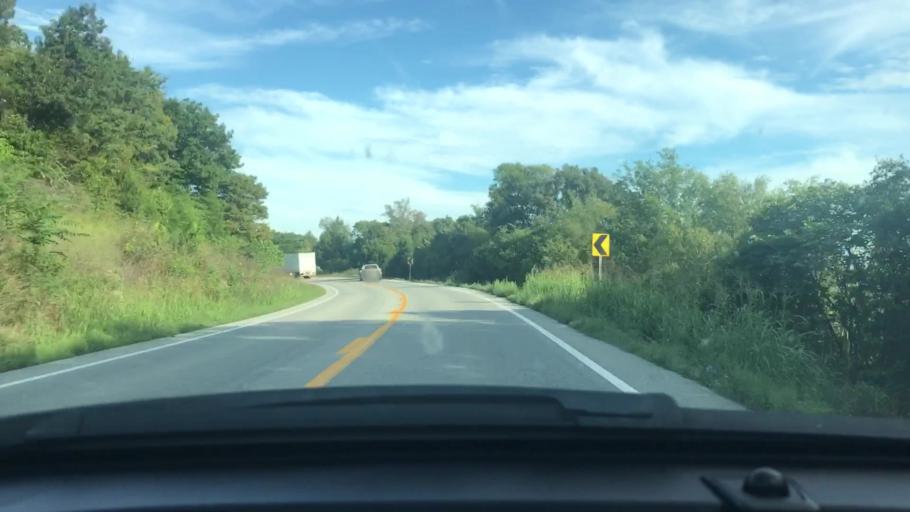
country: US
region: Arkansas
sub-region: Sharp County
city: Cherokee Village
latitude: 36.2977
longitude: -91.4373
